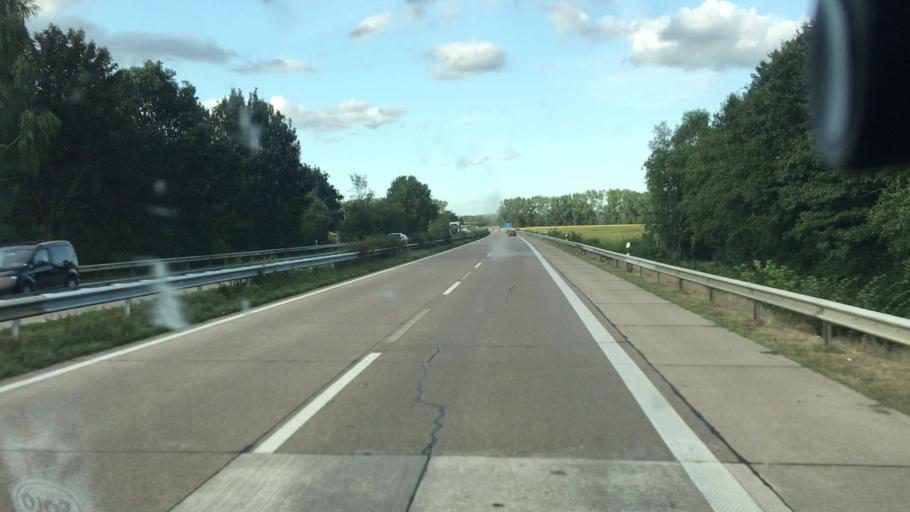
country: DE
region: Lower Saxony
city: Wardenburg
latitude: 53.0847
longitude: 8.2564
